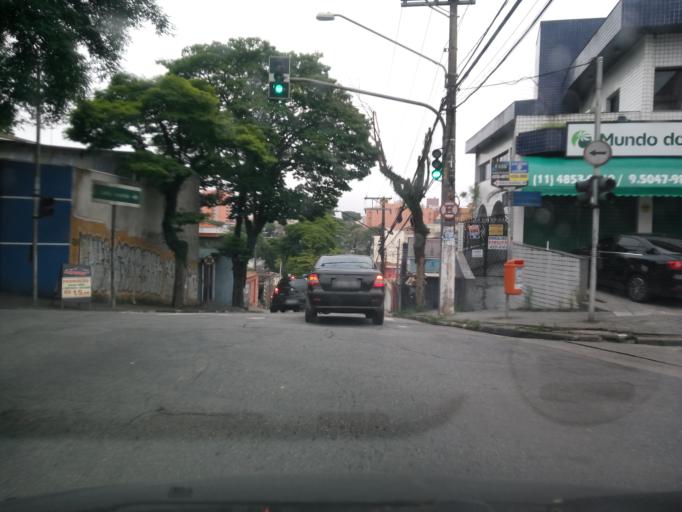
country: BR
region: Sao Paulo
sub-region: Sao Bernardo Do Campo
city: Sao Bernardo do Campo
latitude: -23.7142
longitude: -46.5437
